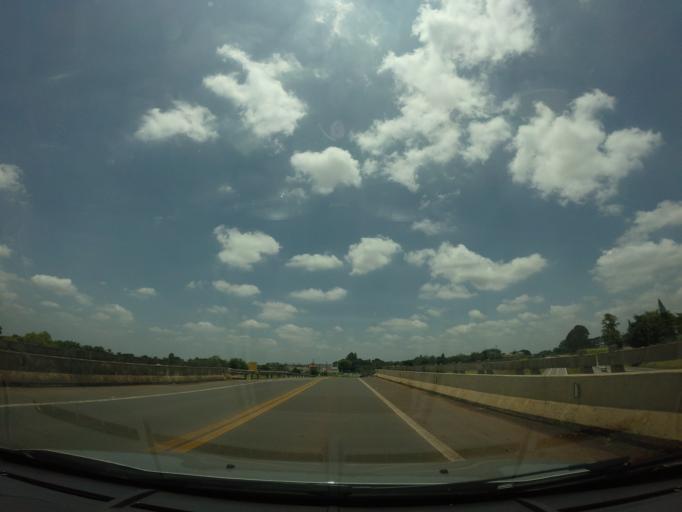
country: BR
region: Sao Paulo
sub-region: Piracicaba
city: Piracicaba
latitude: -22.7646
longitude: -47.5954
